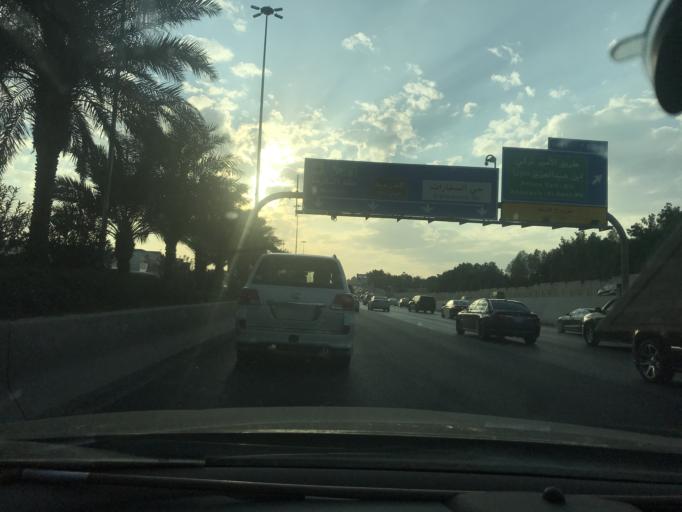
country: SA
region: Ar Riyad
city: Riyadh
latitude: 24.7503
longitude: 46.6217
